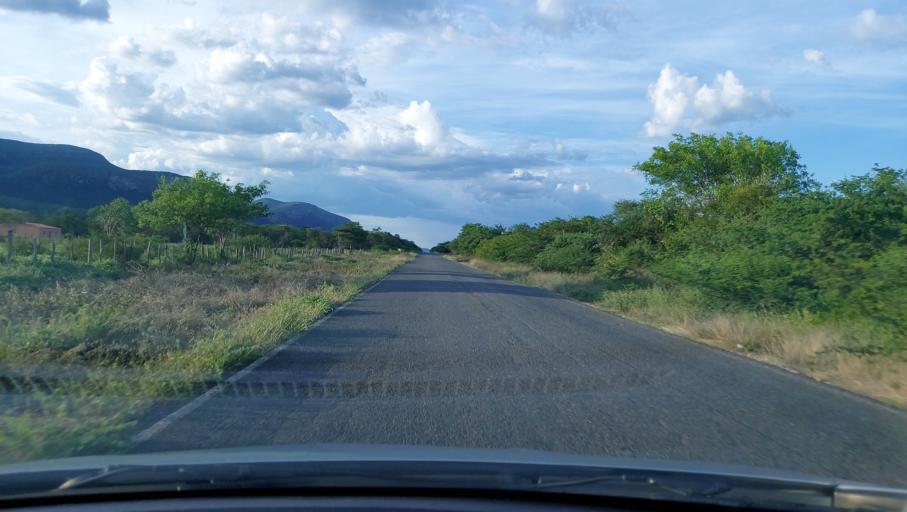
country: BR
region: Bahia
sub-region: Oliveira Dos Brejinhos
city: Beira Rio
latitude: -12.1864
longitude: -42.5397
